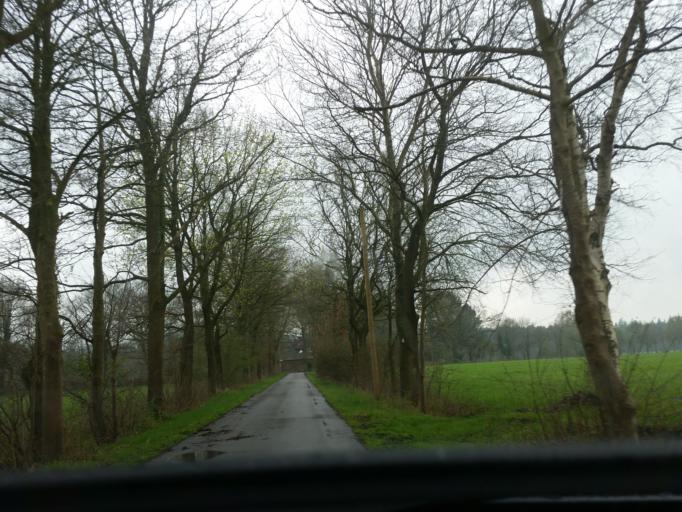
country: DE
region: Lower Saxony
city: Hipstedt
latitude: 53.4760
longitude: 8.9656
